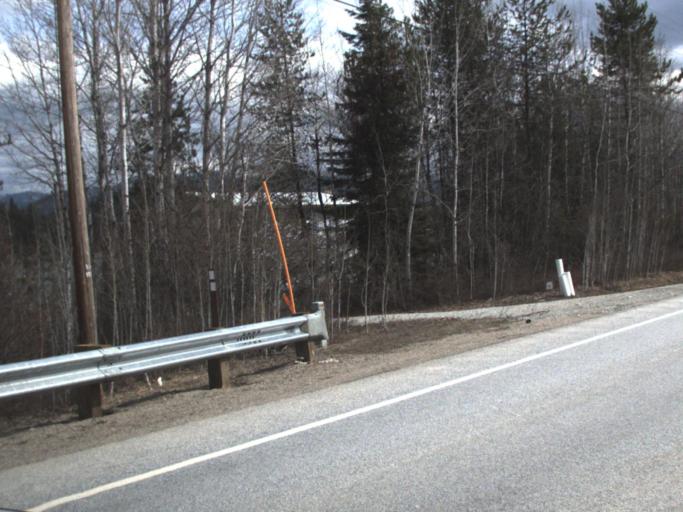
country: US
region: Washington
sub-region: Pend Oreille County
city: Newport
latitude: 48.2318
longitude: -117.2097
